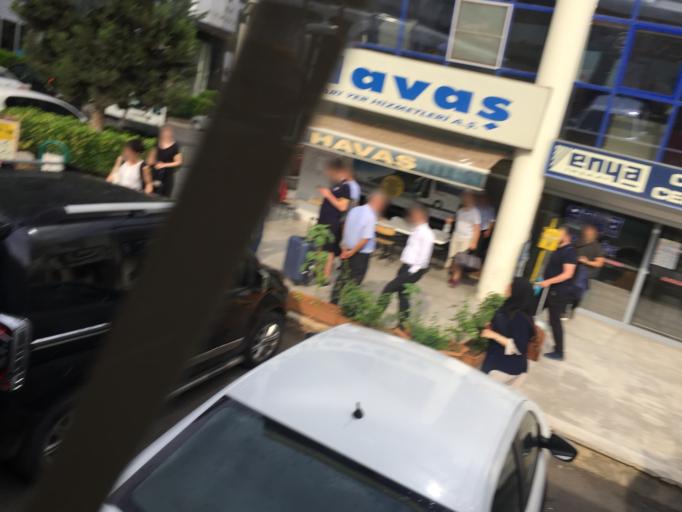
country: TR
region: Gaziantep
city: Gaziantep
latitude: 37.0679
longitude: 37.3715
